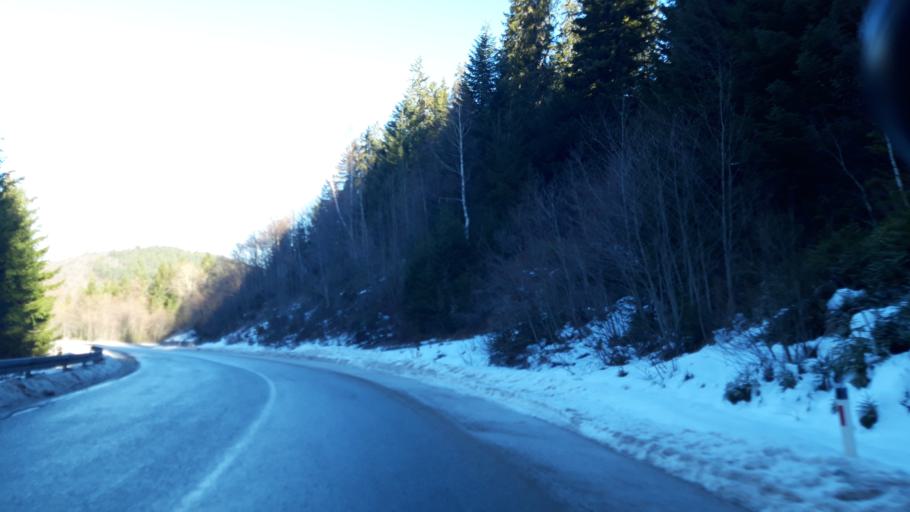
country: BA
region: Republika Srpska
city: Koran
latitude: 43.7813
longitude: 18.5532
